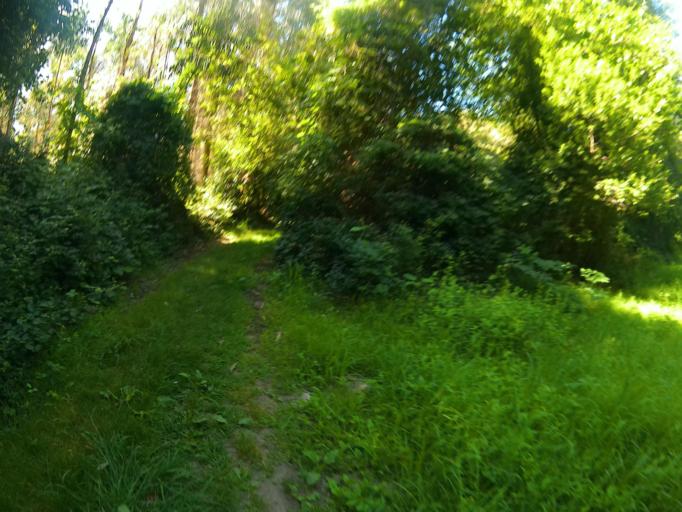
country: PT
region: Viana do Castelo
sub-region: Viana do Castelo
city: Darque
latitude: 41.7199
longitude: -8.6795
